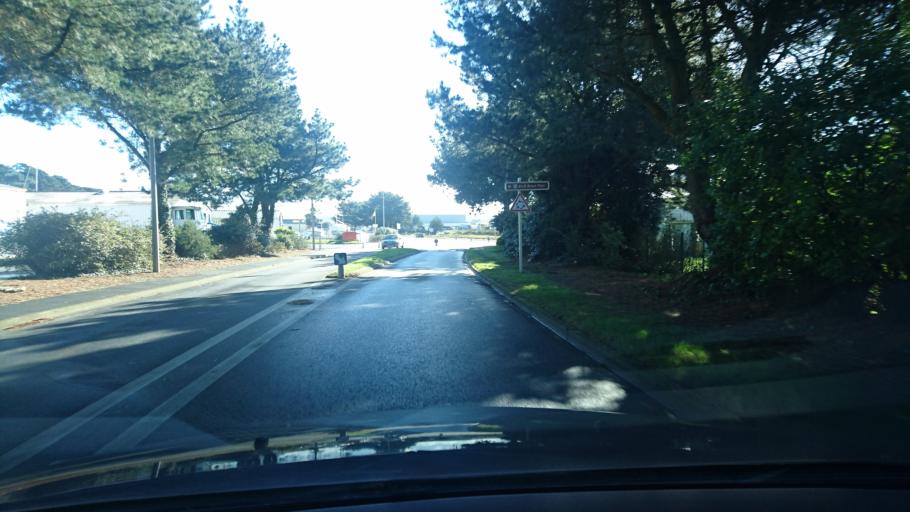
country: FR
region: Brittany
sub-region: Departement du Finistere
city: Brest
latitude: 48.3922
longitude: -4.4467
